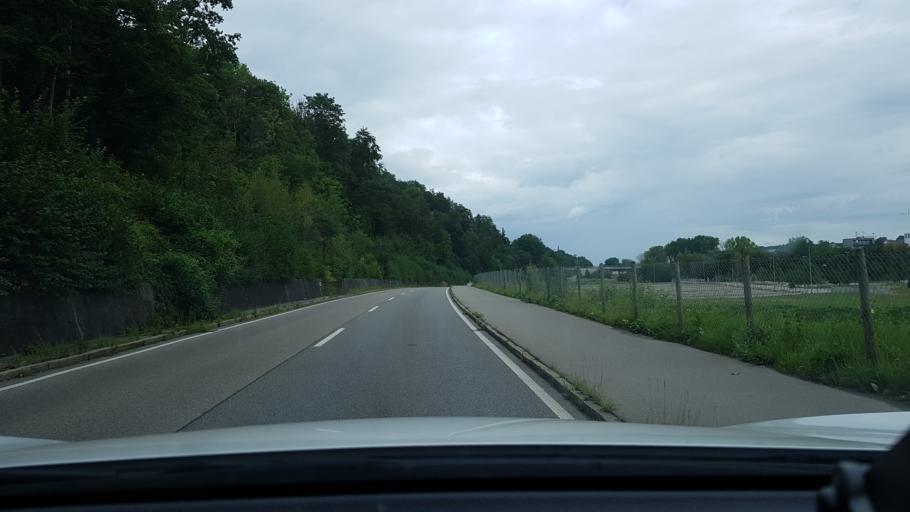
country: DE
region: Baden-Wuerttemberg
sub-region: Tuebingen Region
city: Warthausen
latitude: 48.1127
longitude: 9.7918
